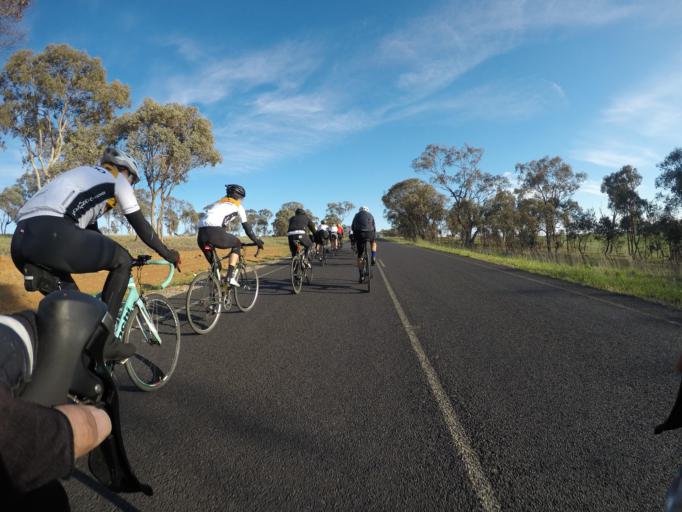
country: AU
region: New South Wales
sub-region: Cabonne
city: Molong
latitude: -32.9771
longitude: 148.7855
